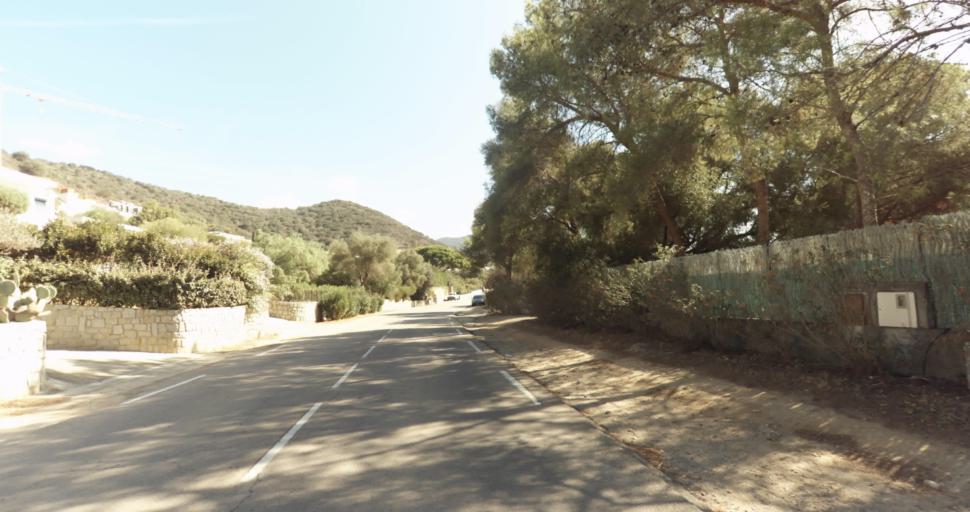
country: FR
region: Corsica
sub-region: Departement de la Corse-du-Sud
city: Ajaccio
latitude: 41.9066
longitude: 8.6286
